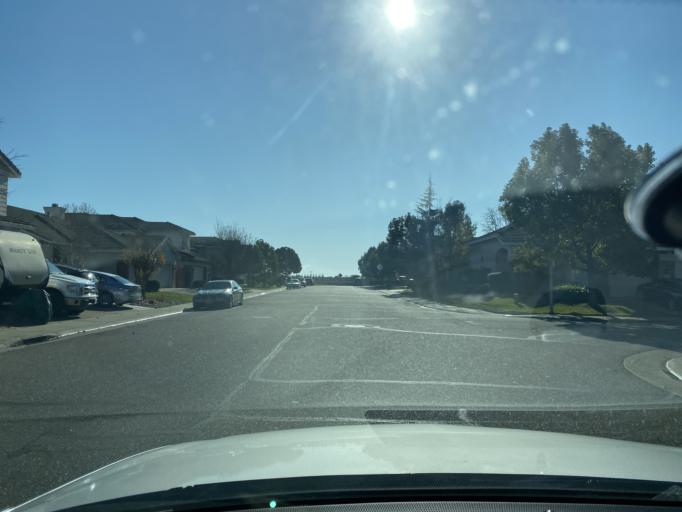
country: US
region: California
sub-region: Sacramento County
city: Elk Grove
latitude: 38.4345
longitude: -121.3928
